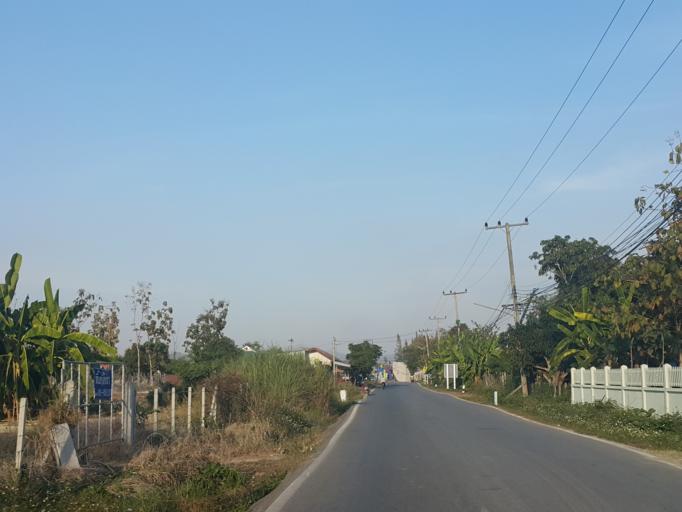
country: TH
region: Chiang Mai
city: San Sai
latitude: 18.8219
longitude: 99.0767
